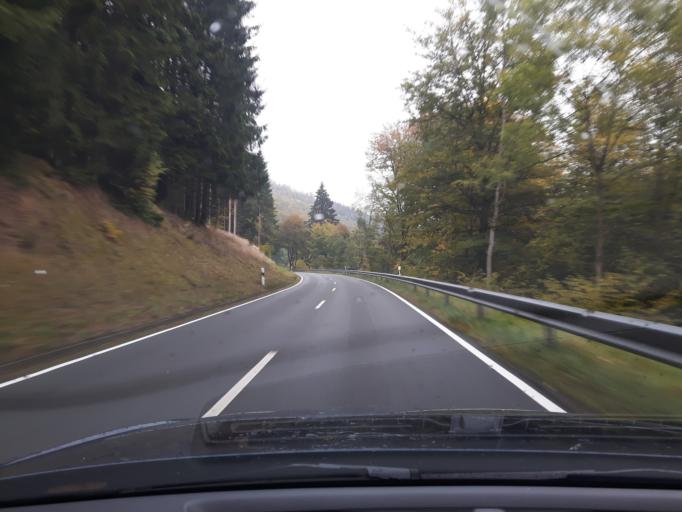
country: DE
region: North Rhine-Westphalia
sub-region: Regierungsbezirk Arnsberg
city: Bad Laasphe
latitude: 50.9588
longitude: 8.3922
